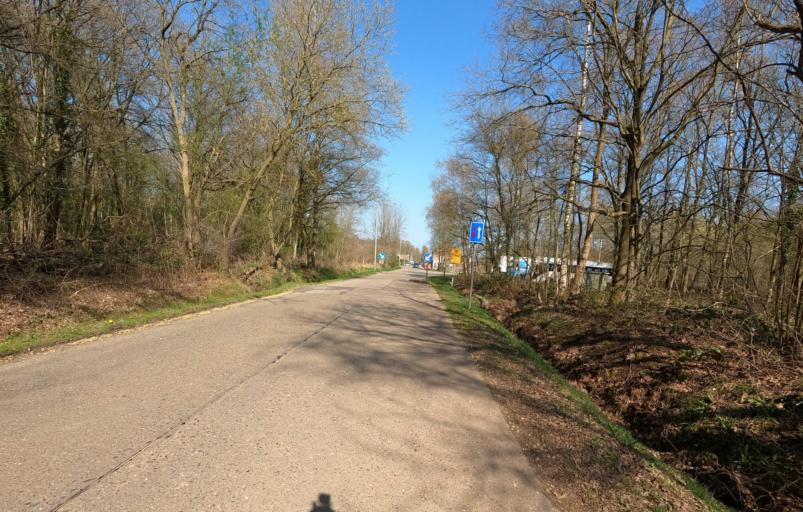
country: BE
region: Flanders
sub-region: Provincie Antwerpen
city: Rijkevorsel
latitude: 51.3283
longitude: 4.7988
